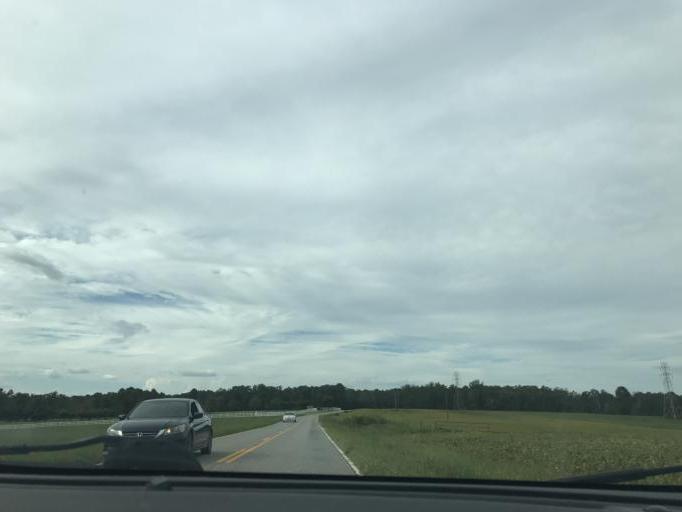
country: US
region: South Carolina
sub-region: Cherokee County
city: Gaffney
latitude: 35.1529
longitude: -81.6984
